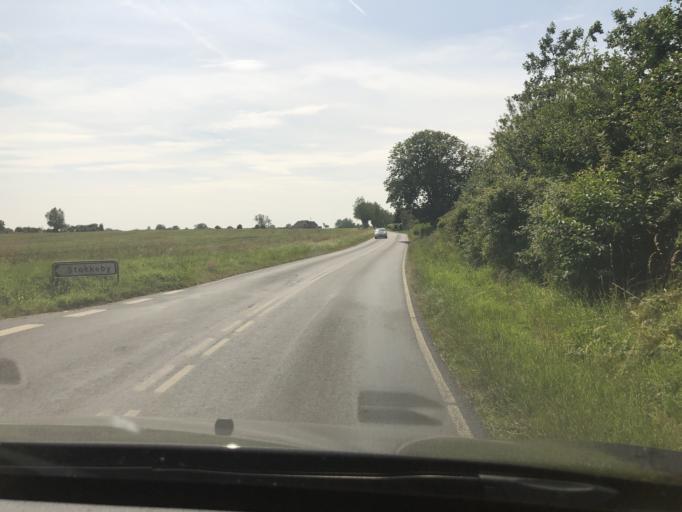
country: DK
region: South Denmark
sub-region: AEro Kommune
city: AEroskobing
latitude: 54.8703
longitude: 10.3918
